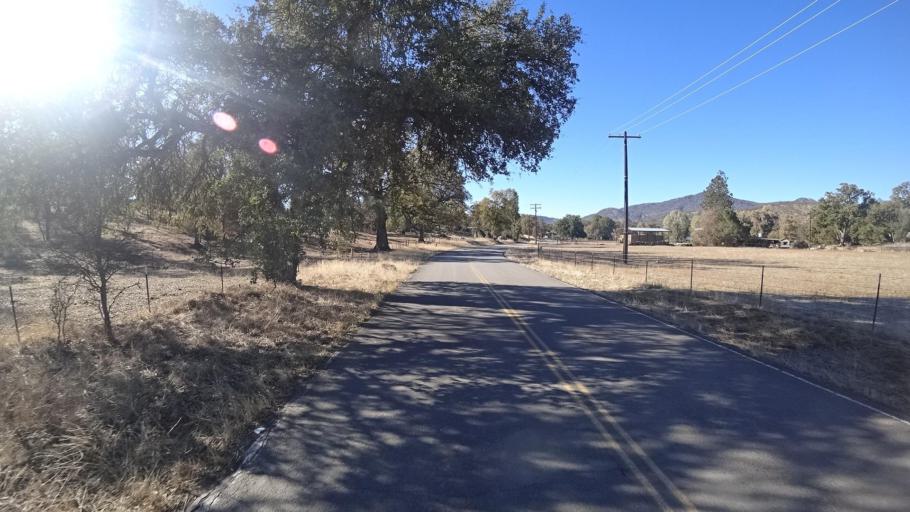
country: US
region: California
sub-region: Kern County
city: Alta Sierra
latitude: 35.7726
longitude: -118.7083
